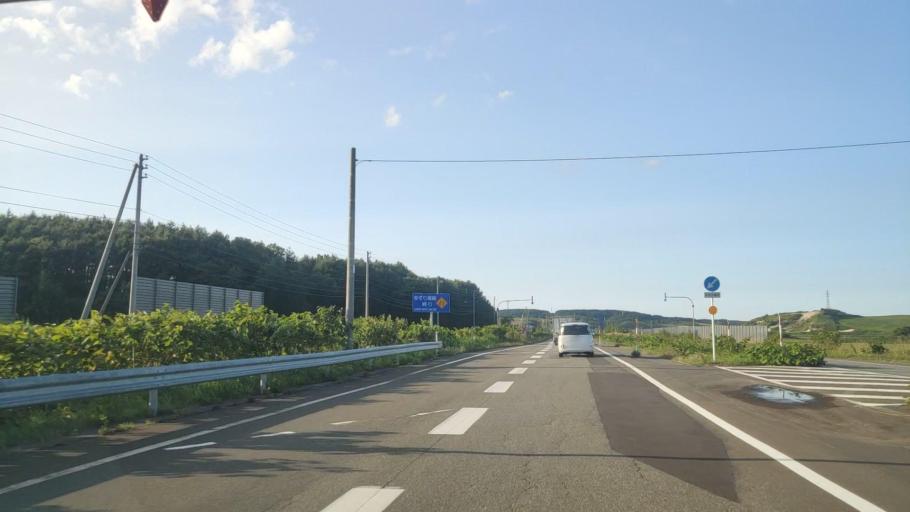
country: JP
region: Hokkaido
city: Wakkanai
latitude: 45.3237
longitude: 141.7195
